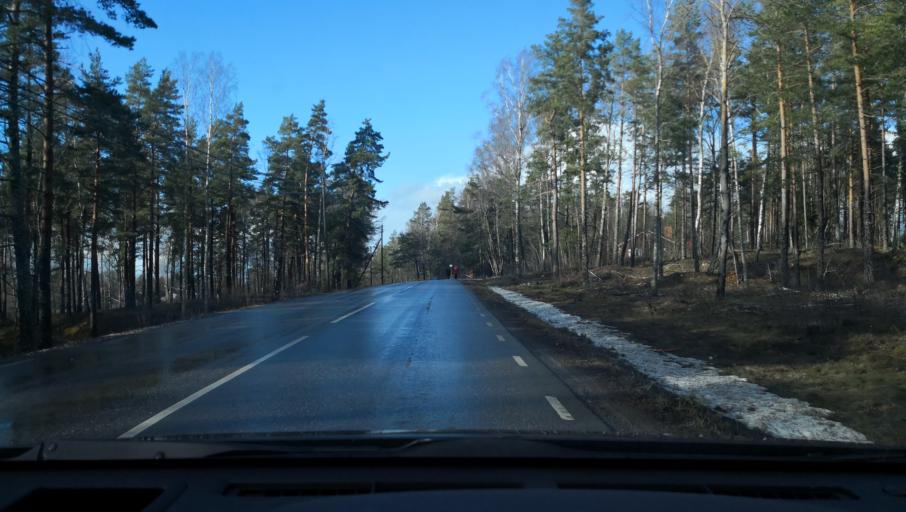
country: SE
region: Vaestmanland
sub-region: Arboga Kommun
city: Arboga
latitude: 59.3755
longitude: 15.8423
